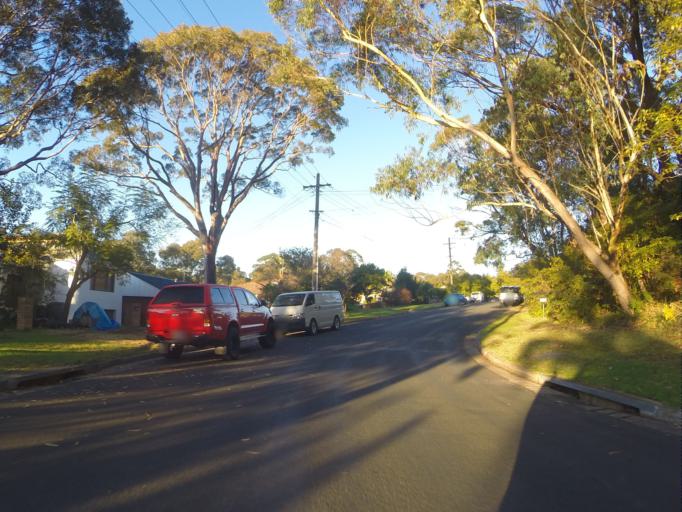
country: AU
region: New South Wales
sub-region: Sutherland Shire
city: Engadine
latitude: -34.0547
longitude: 151.0087
